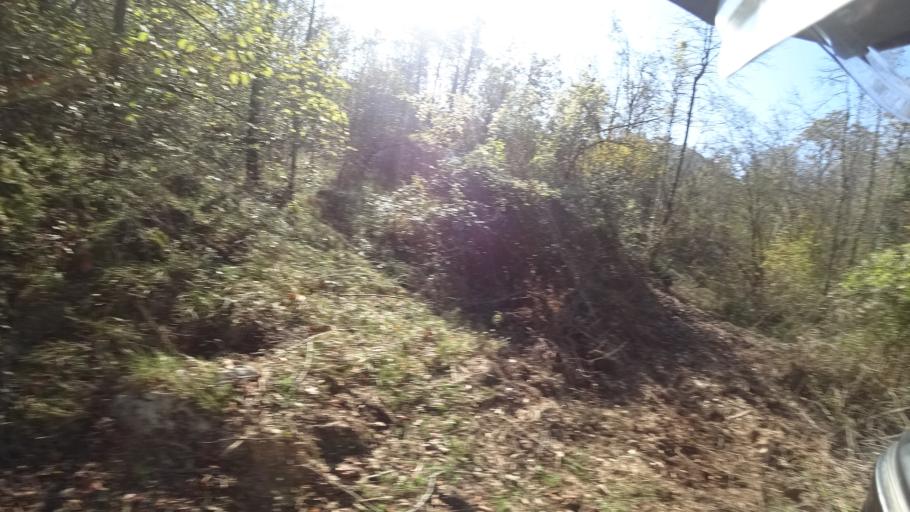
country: HR
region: Primorsko-Goranska
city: Matulji
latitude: 45.3904
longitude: 14.2986
